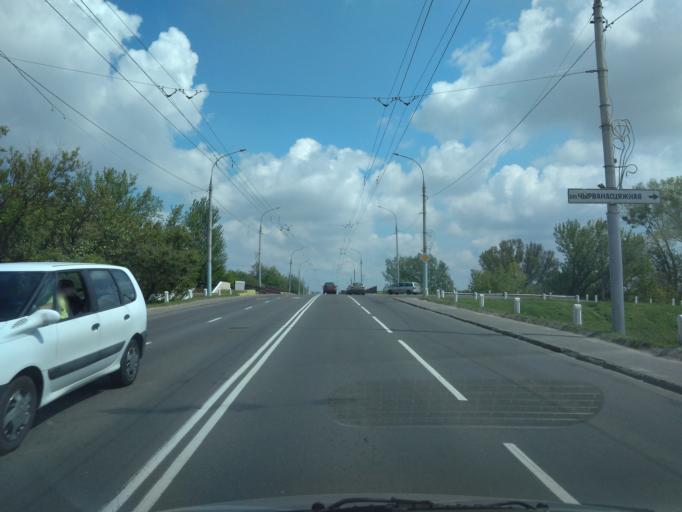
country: BY
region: Brest
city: Brest
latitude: 52.0899
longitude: 23.7138
